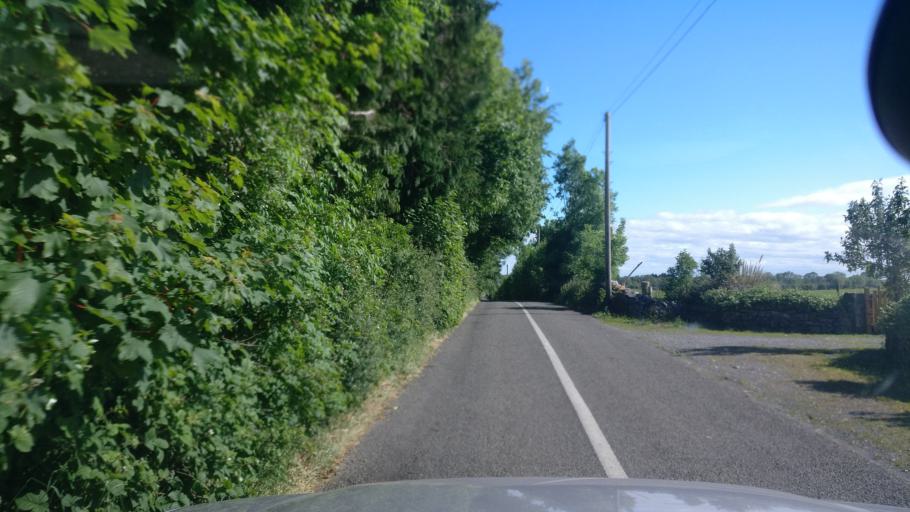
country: IE
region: Connaught
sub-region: County Galway
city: Loughrea
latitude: 53.2361
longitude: -8.6235
